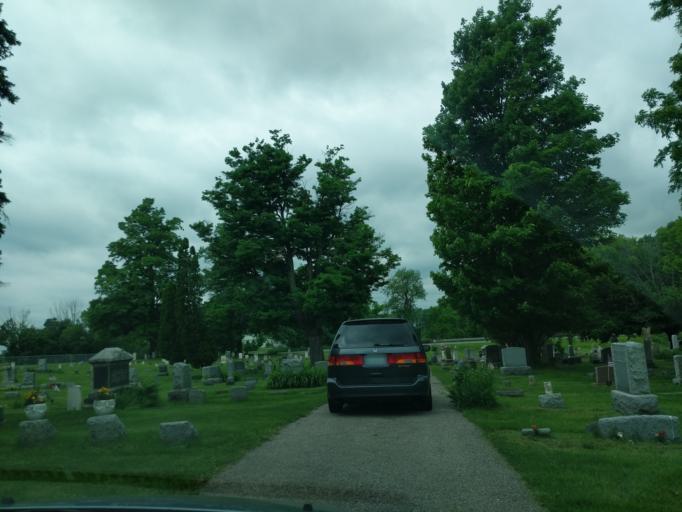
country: US
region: Michigan
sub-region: Ingham County
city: Webberville
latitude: 42.6946
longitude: -84.2192
